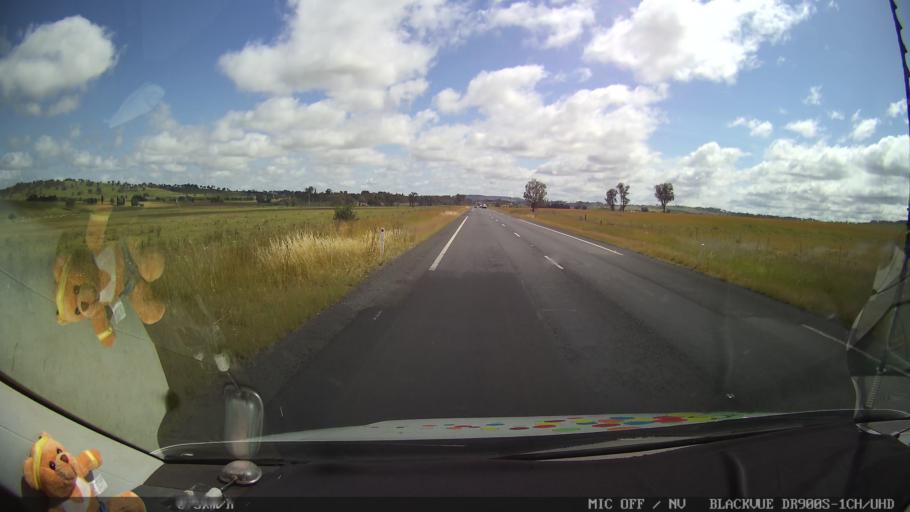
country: AU
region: New South Wales
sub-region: Glen Innes Severn
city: Glen Innes
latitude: -29.9445
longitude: 151.7207
